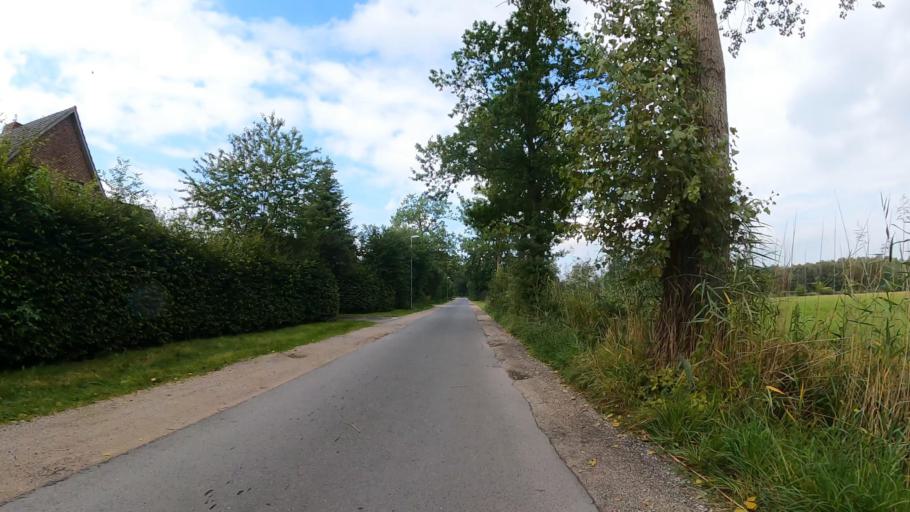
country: DE
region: Schleswig-Holstein
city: Tornesch
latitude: 53.7127
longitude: 9.7115
